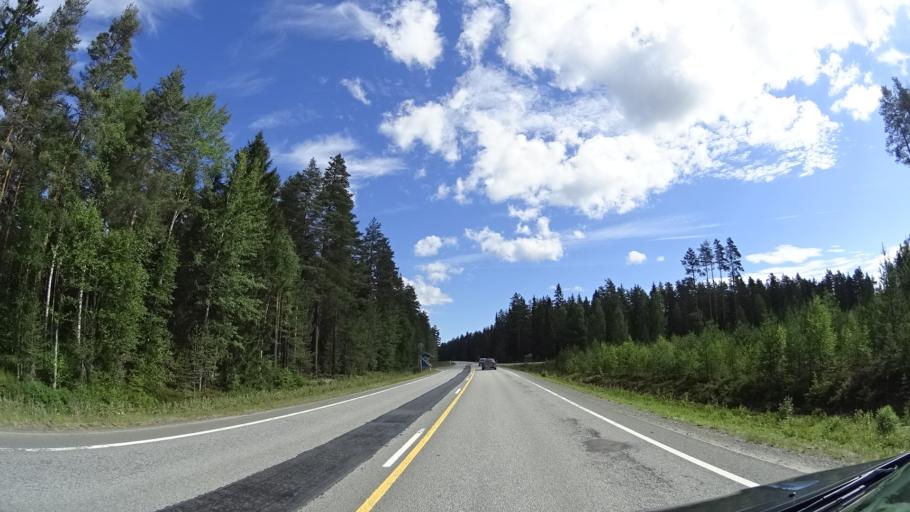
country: FI
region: Pirkanmaa
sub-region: Luoteis-Pirkanmaa
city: Kihnioe
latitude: 62.1328
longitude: 23.1360
